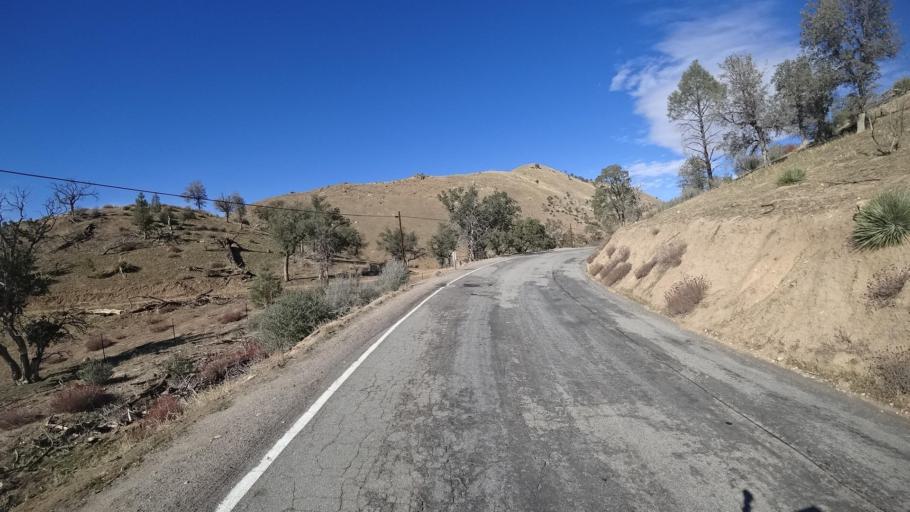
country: US
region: California
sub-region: Kern County
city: Bodfish
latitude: 35.5584
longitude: -118.5107
